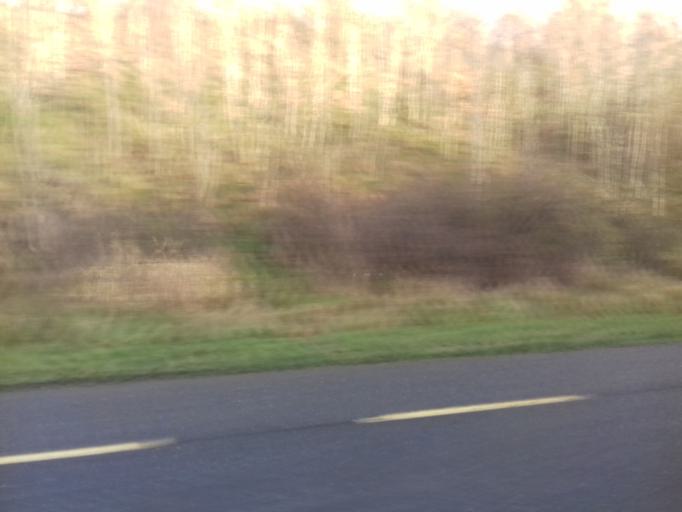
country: IE
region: Ulster
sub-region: County Monaghan
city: Carrickmacross
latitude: 53.9776
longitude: -6.7045
